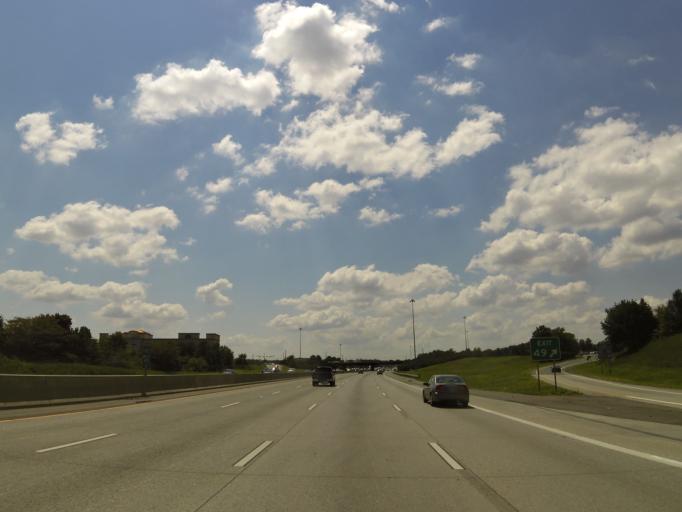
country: US
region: North Carolina
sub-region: Cabarrus County
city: Harrisburg
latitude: 35.3722
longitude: -80.7110
